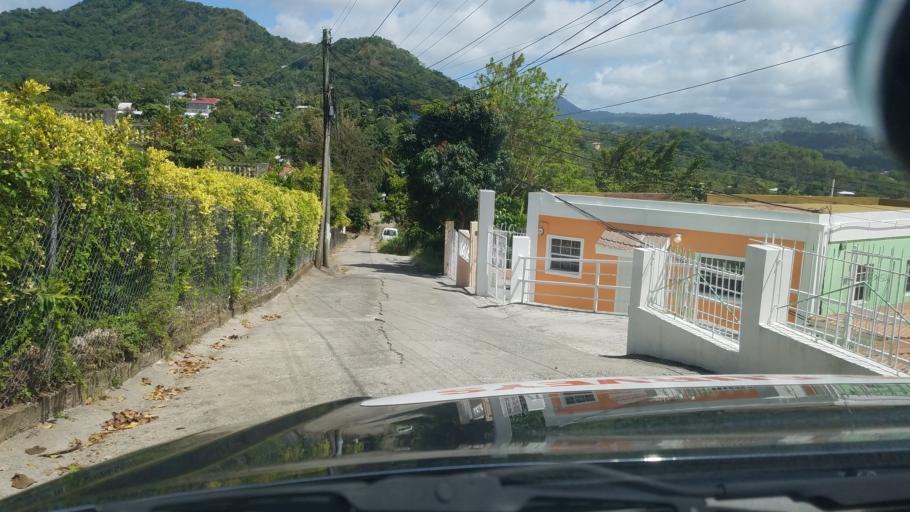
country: LC
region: Castries Quarter
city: Bisee
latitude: 14.0313
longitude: -60.9525
